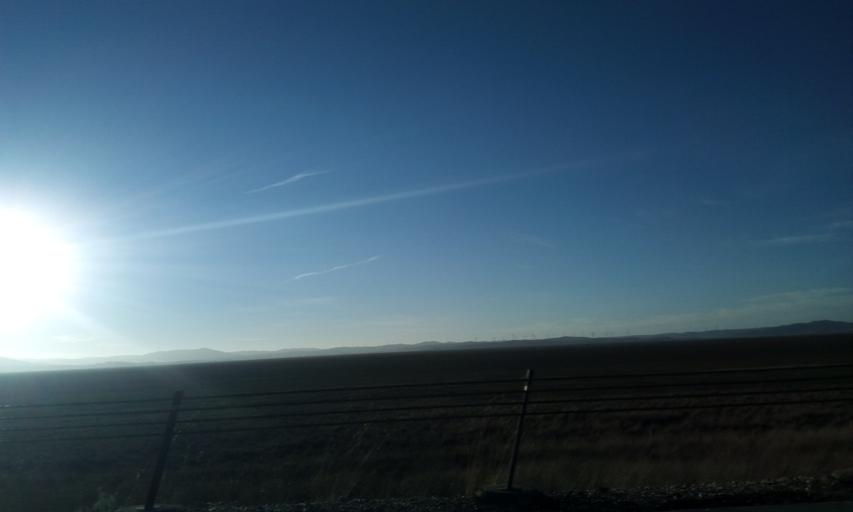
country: AU
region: New South Wales
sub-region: Yass Valley
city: Gundaroo
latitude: -35.0584
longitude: 149.3748
